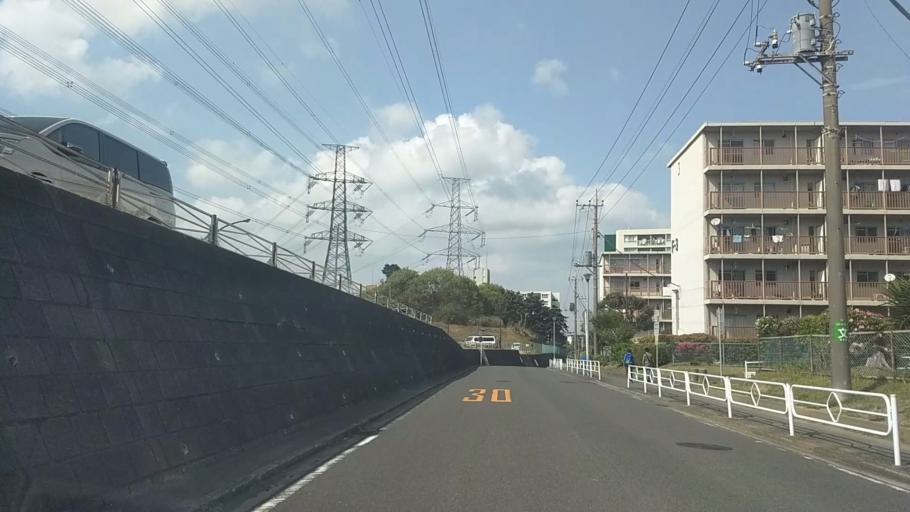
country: JP
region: Kanagawa
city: Kamakura
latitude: 35.3839
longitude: 139.5682
